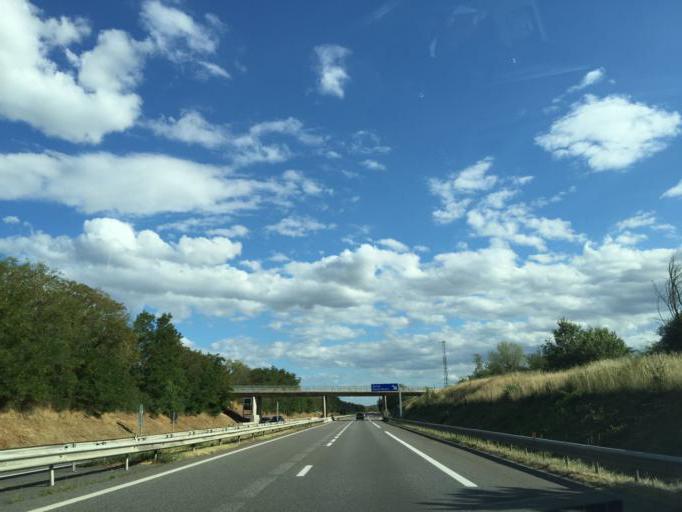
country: FR
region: Rhone-Alpes
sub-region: Departement de la Loire
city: Montrond-les-Bains
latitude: 45.6101
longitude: 4.2070
